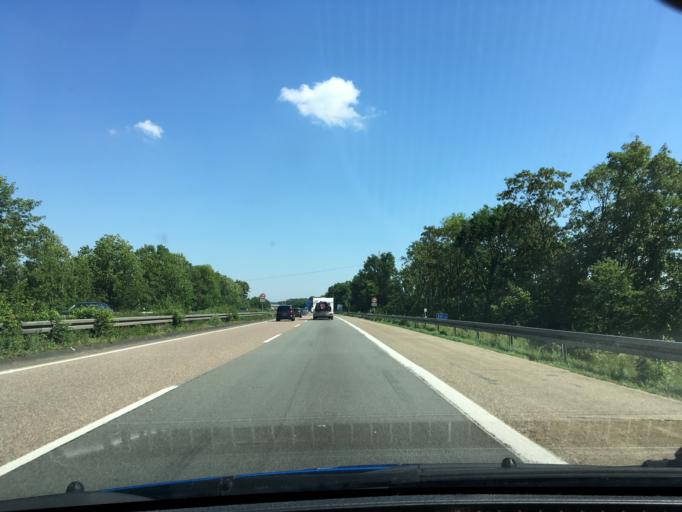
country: DE
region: Lower Saxony
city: Hasbergen
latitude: 52.2540
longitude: 7.9166
